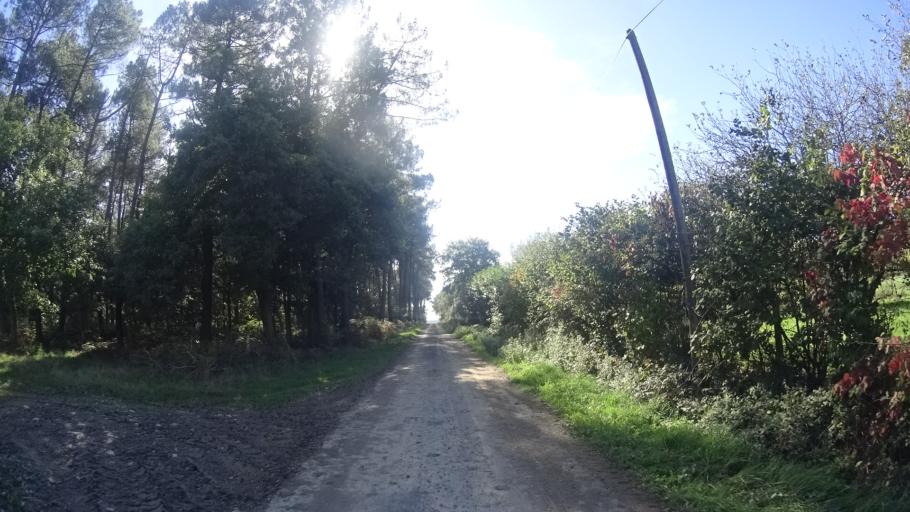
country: FR
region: Brittany
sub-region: Departement du Morbihan
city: La Gacilly
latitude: 47.7488
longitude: -2.1688
